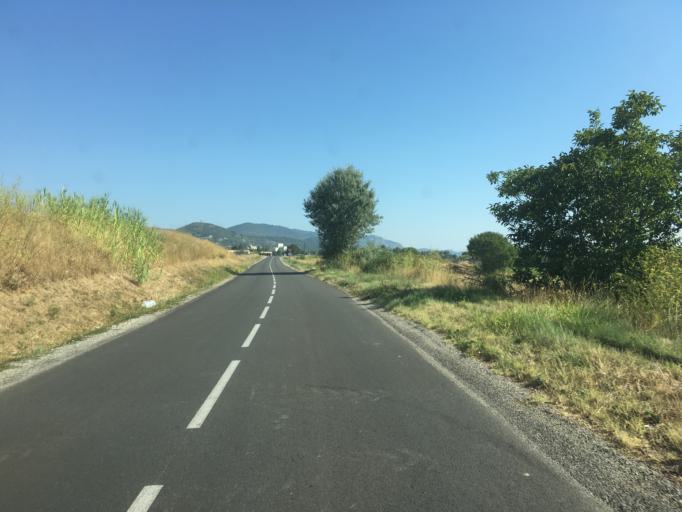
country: FR
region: Provence-Alpes-Cote d'Azur
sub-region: Departement des Alpes-de-Haute-Provence
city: Manosque
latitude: 43.8080
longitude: 5.7912
